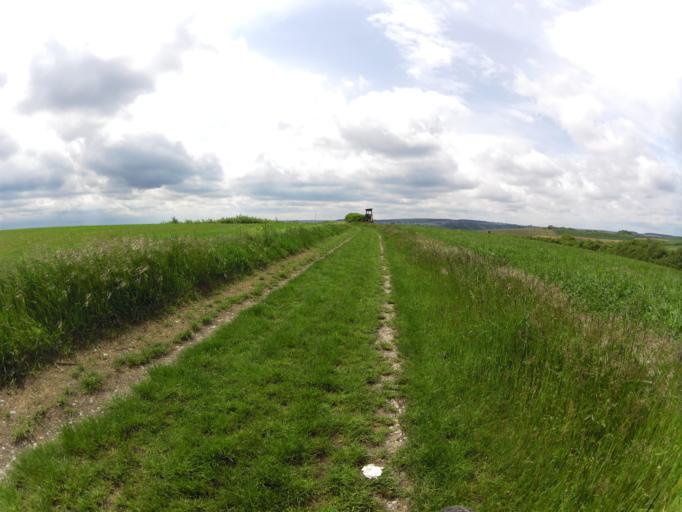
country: DE
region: Bavaria
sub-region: Regierungsbezirk Unterfranken
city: Volkach
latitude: 49.8807
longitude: 10.2194
